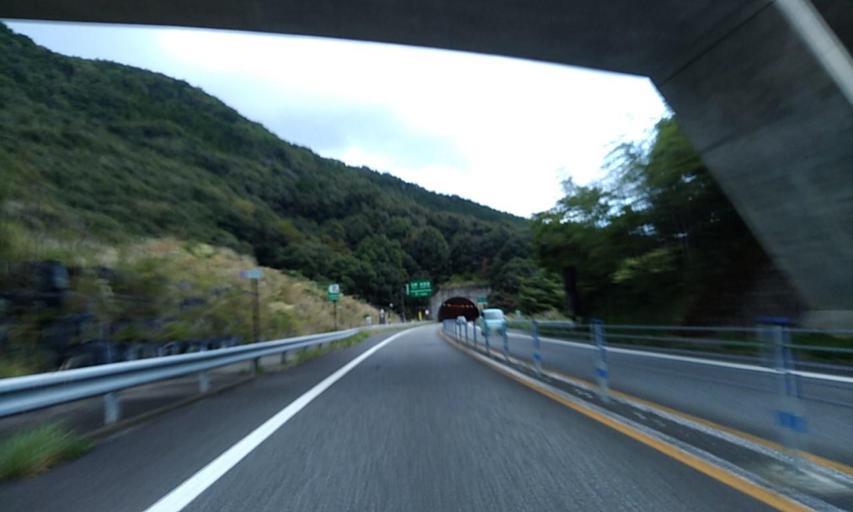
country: JP
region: Wakayama
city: Shingu
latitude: 33.6868
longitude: 135.9555
